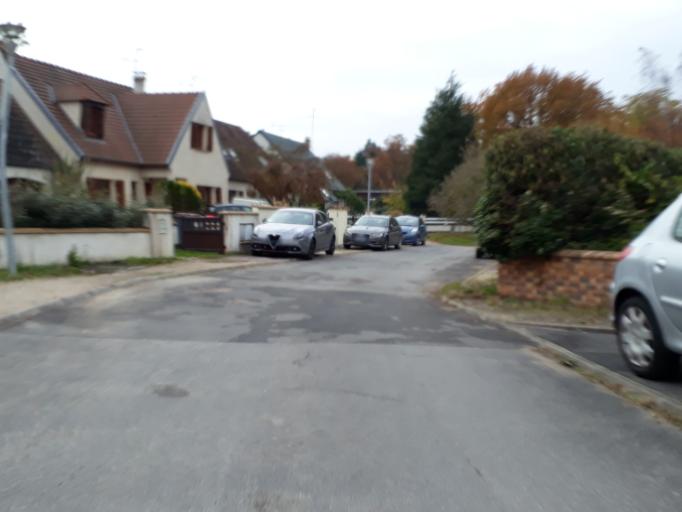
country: FR
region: Ile-de-France
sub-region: Departement de Seine-et-Marne
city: Bois-le-Roi
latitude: 48.4773
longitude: 2.7077
